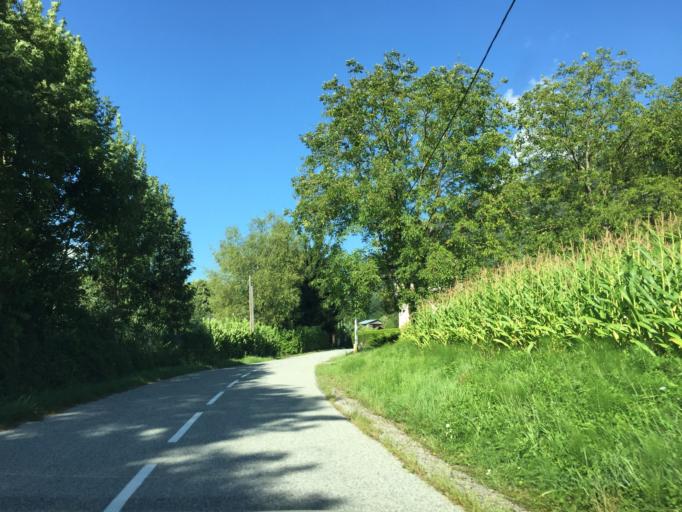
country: FR
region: Rhone-Alpes
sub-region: Departement de la Savoie
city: Coise-Saint-Jean-Pied-Gauthier
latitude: 45.4895
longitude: 6.1555
